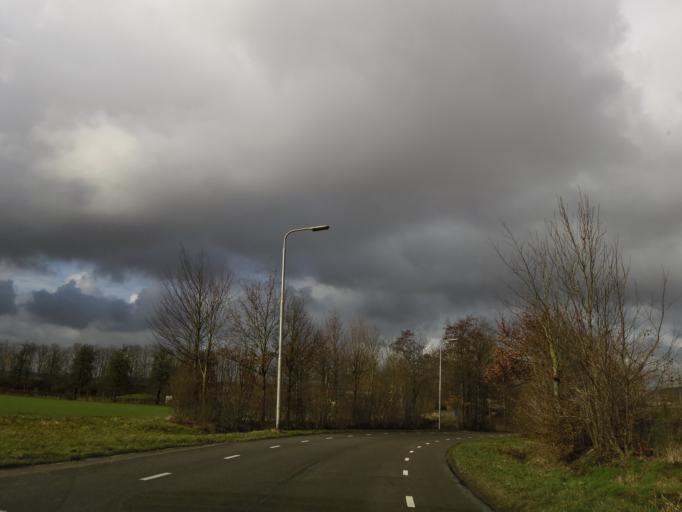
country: NL
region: Limburg
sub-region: Eijsden-Margraten
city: Eijsden
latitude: 50.7820
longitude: 5.7323
